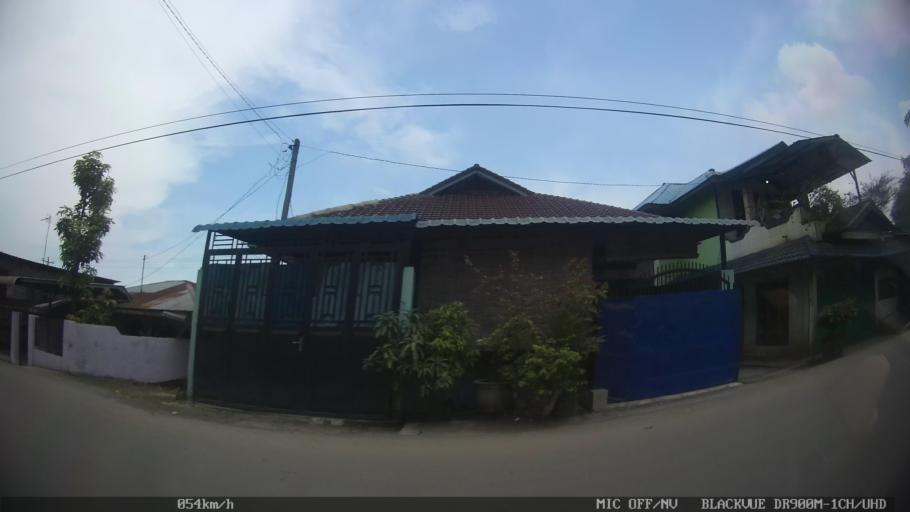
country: ID
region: North Sumatra
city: Labuhan Deli
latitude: 3.6947
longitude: 98.6729
